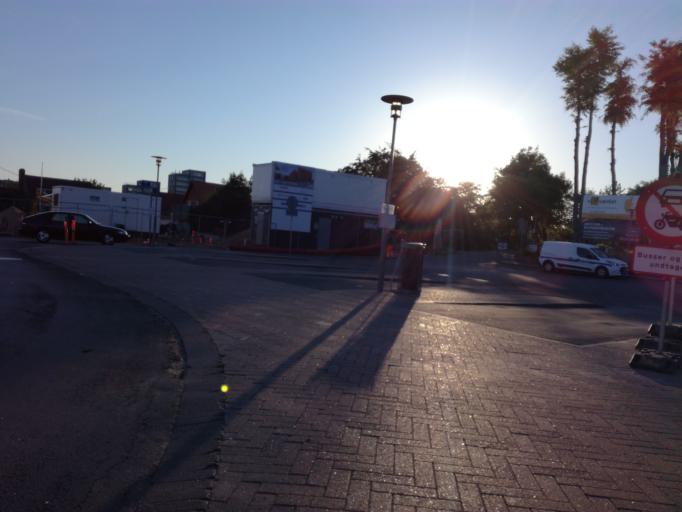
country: DK
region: South Denmark
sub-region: Middelfart Kommune
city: Middelfart
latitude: 55.5021
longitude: 9.7343
